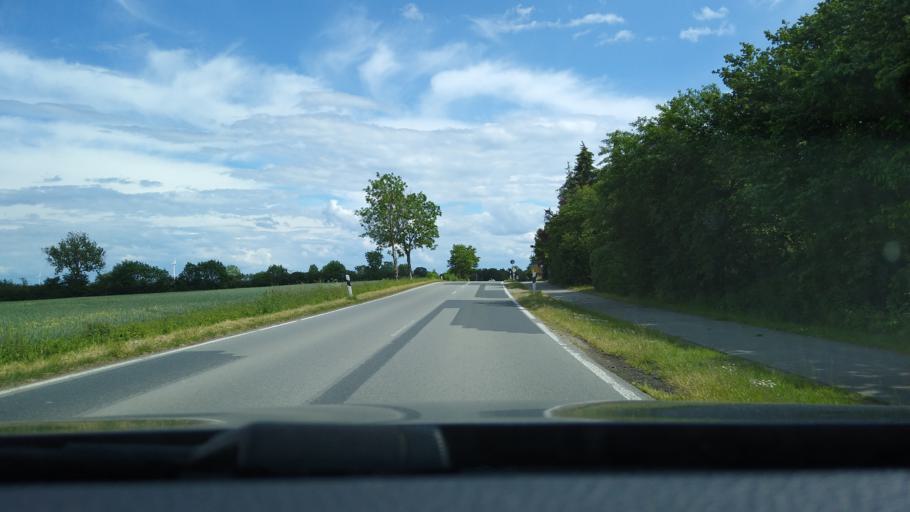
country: DE
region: Schleswig-Holstein
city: Kabelhorst
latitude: 54.2139
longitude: 10.9412
